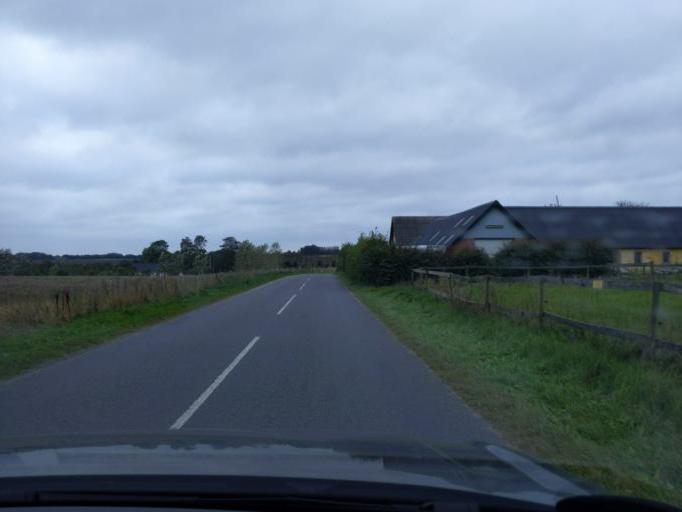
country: DK
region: Central Jutland
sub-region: Viborg Kommune
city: Bjerringbro
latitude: 56.5384
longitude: 9.6036
